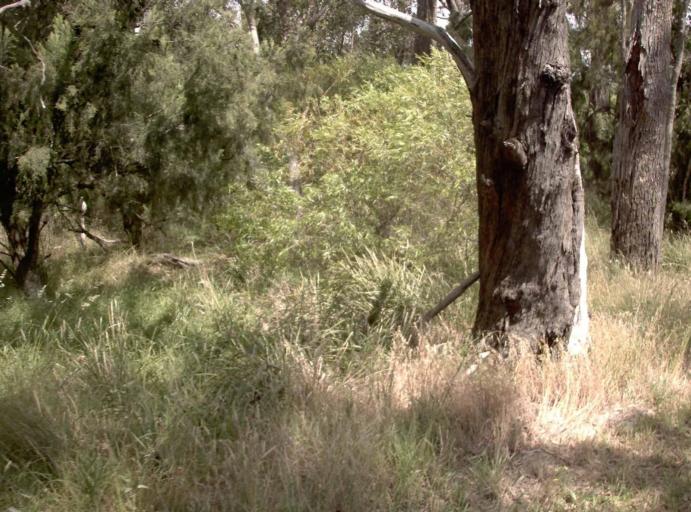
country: AU
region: Victoria
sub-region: Latrobe
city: Traralgon
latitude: -38.2944
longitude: 146.5385
